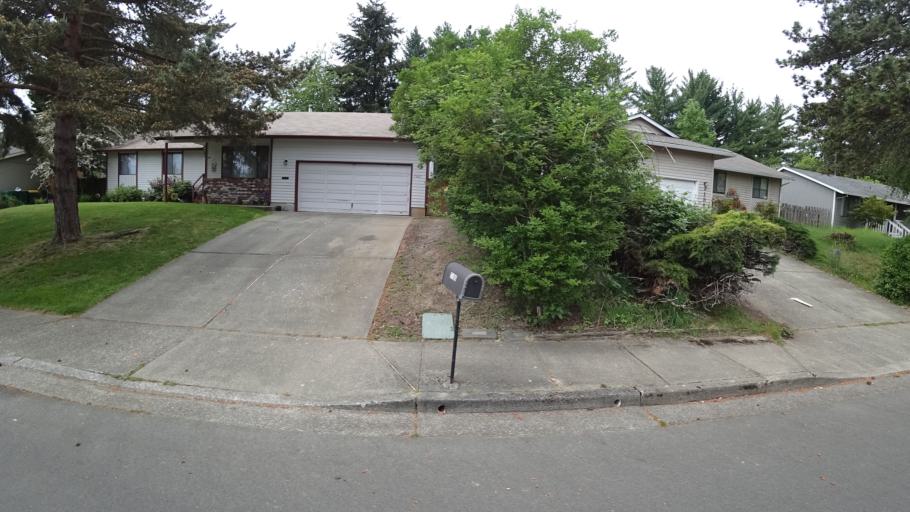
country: US
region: Oregon
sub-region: Washington County
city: Aloha
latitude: 45.4681
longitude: -122.8420
